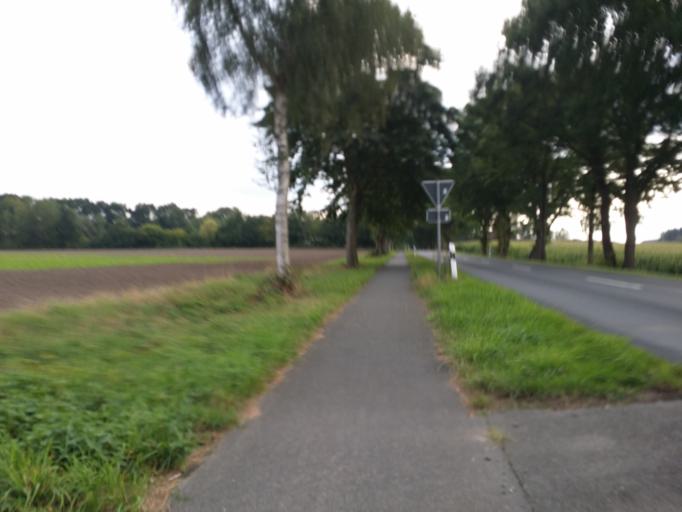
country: DE
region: Lower Saxony
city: Bremervorde
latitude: 53.4688
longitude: 9.1283
